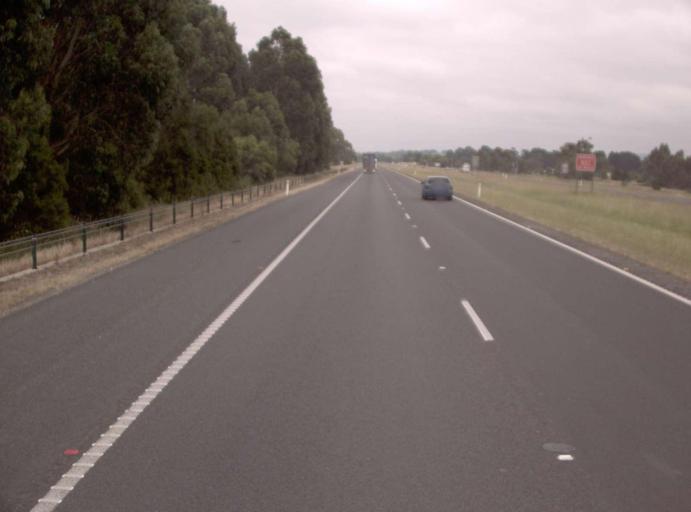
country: AU
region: Victoria
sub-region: Cardinia
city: Bunyip
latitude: -38.0867
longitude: 145.7754
